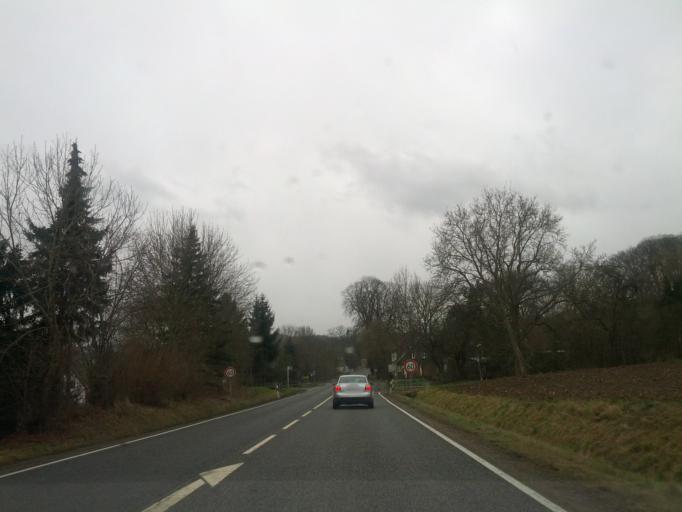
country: DE
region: Lower Saxony
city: Gemeinde Friedland
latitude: 51.3893
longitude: 9.9080
